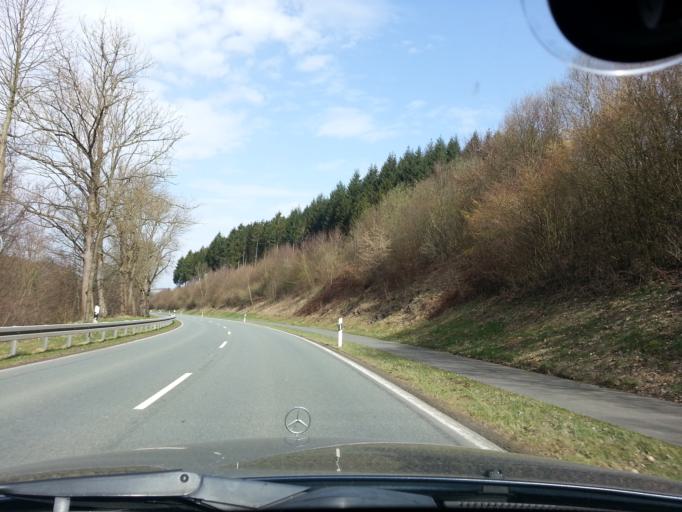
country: DE
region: North Rhine-Westphalia
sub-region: Regierungsbezirk Arnsberg
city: Meschede
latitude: 51.2862
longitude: 8.3317
